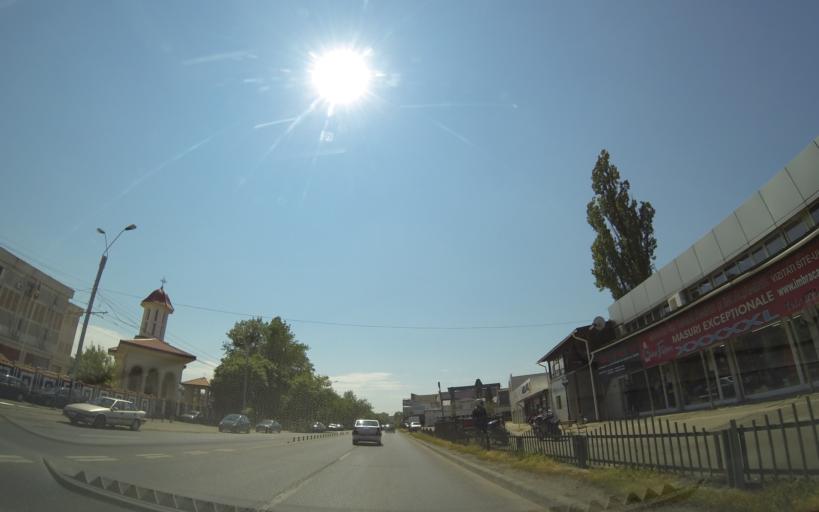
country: RO
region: Bucuresti
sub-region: Municipiul Bucuresti
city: Bucuresti
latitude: 44.4217
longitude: 26.0706
